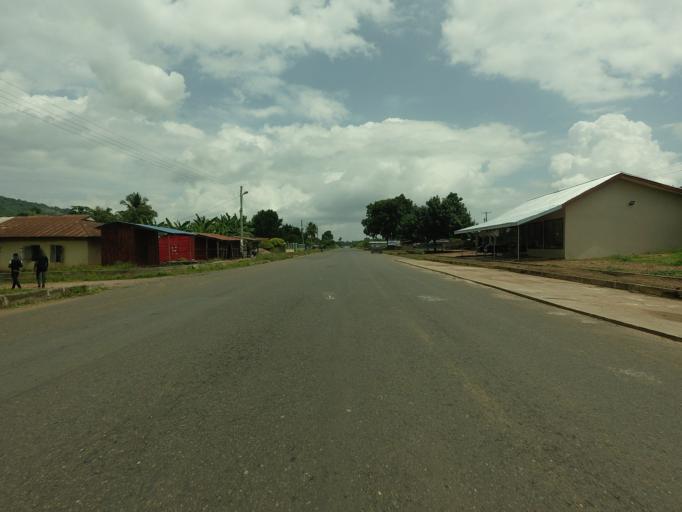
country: GH
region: Volta
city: Ho
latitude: 6.5309
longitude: 0.2275
